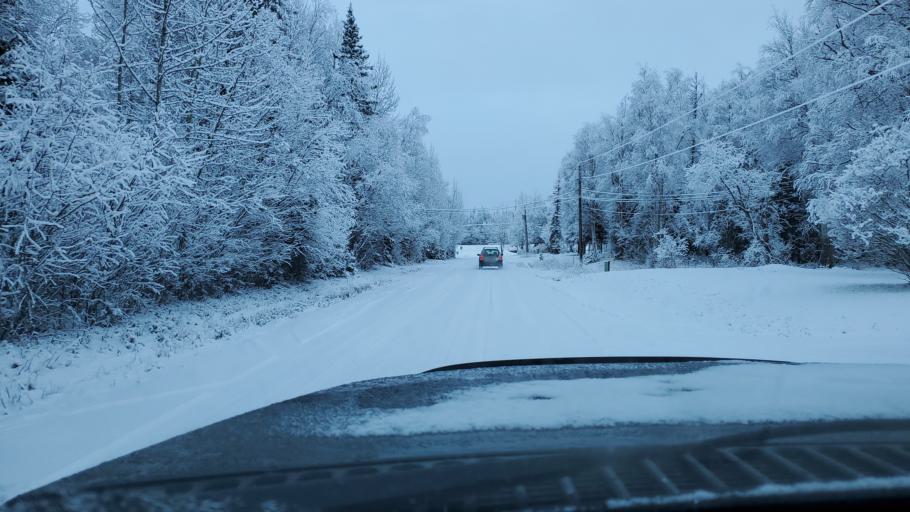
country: US
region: Alaska
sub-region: Matanuska-Susitna Borough
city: Wasilla
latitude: 61.5911
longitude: -149.4133
